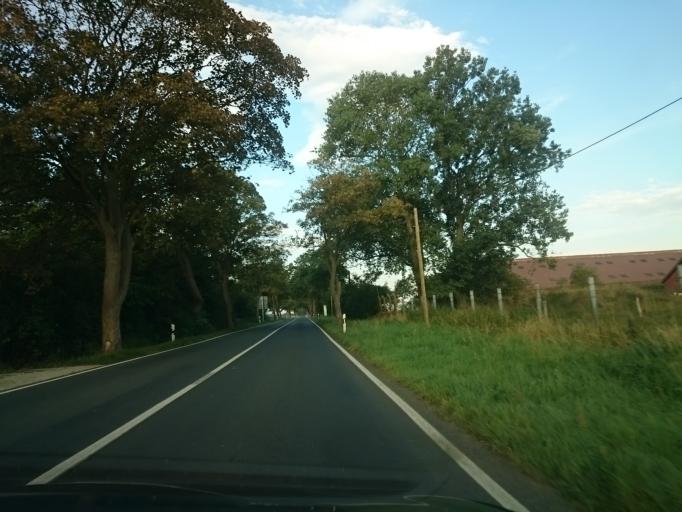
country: DE
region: Mecklenburg-Vorpommern
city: Gross Kiesow
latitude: 53.9473
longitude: 13.4884
